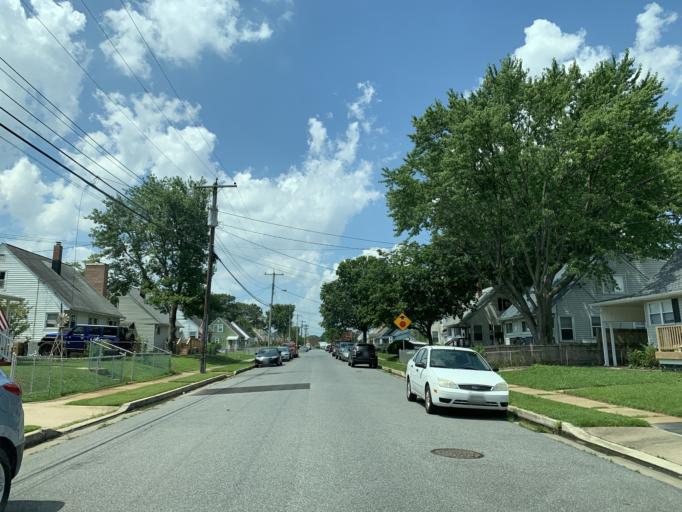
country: US
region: Maryland
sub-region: Baltimore County
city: Essex
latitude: 39.3041
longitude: -76.4573
